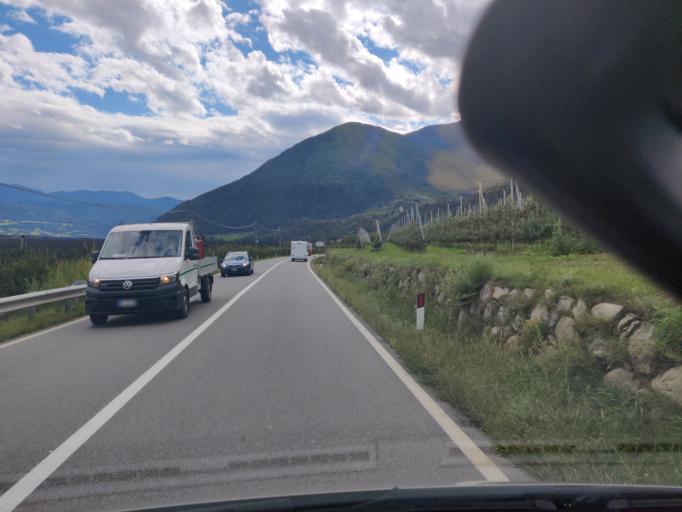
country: IT
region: Trentino-Alto Adige
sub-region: Bolzano
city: Varna
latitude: 46.7569
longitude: 11.6377
